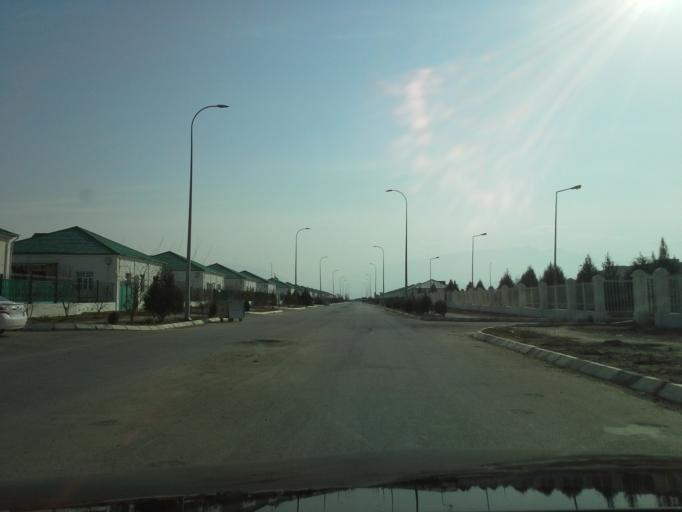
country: TM
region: Ahal
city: Abadan
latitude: 38.1696
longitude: 58.0489
